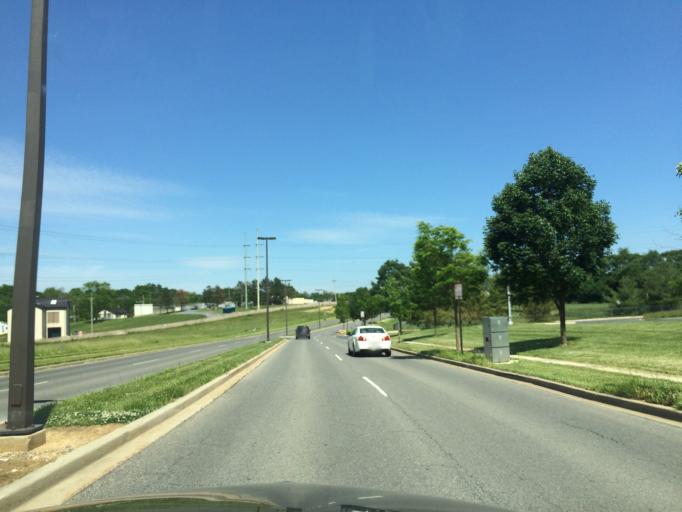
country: US
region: Maryland
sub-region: Frederick County
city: Frederick
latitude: 39.4381
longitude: -77.3976
